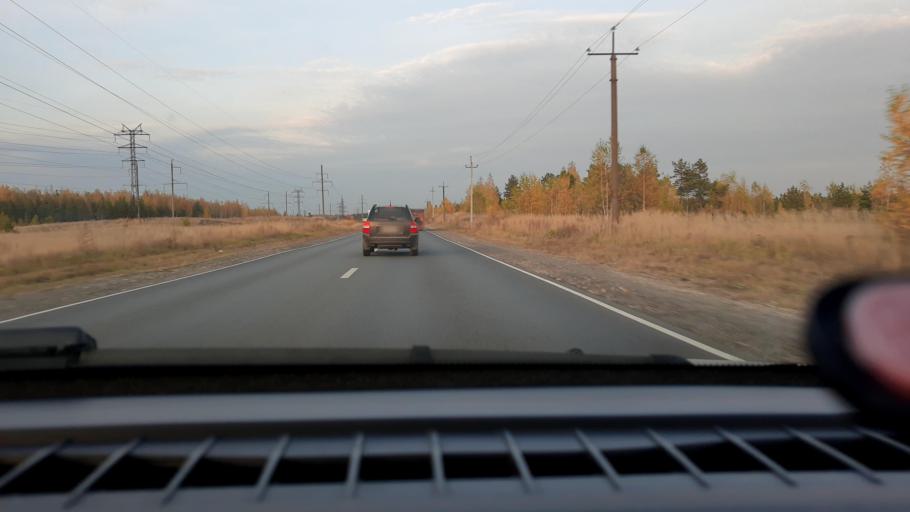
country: RU
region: Nizjnij Novgorod
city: Babino
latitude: 56.3308
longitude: 43.5661
